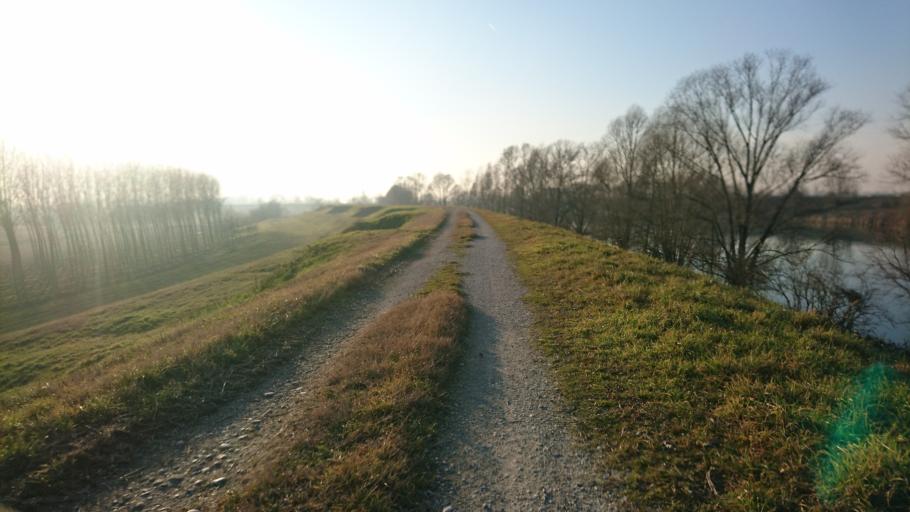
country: IT
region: Veneto
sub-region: Provincia di Rovigo
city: Mardimago
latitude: 45.1227
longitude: 11.8151
